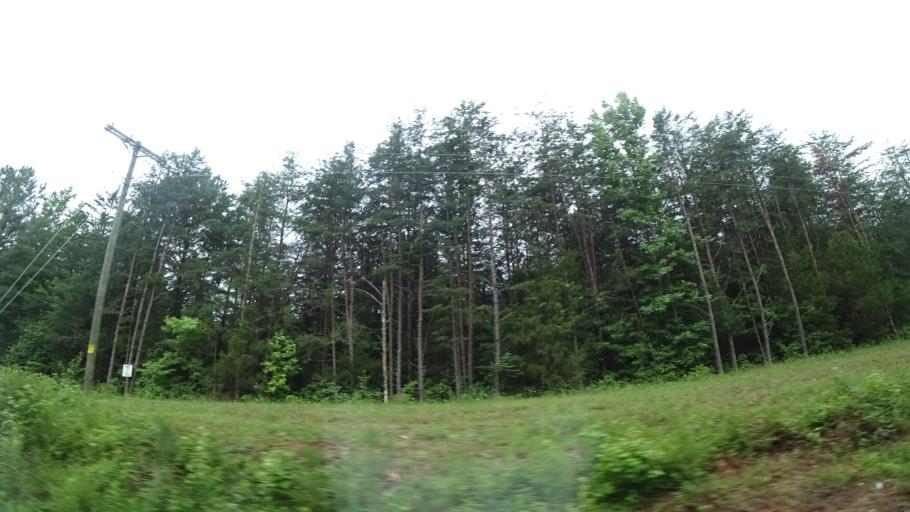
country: US
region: Virginia
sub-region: Spotsylvania County
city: Spotsylvania
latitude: 38.1353
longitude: -77.7912
